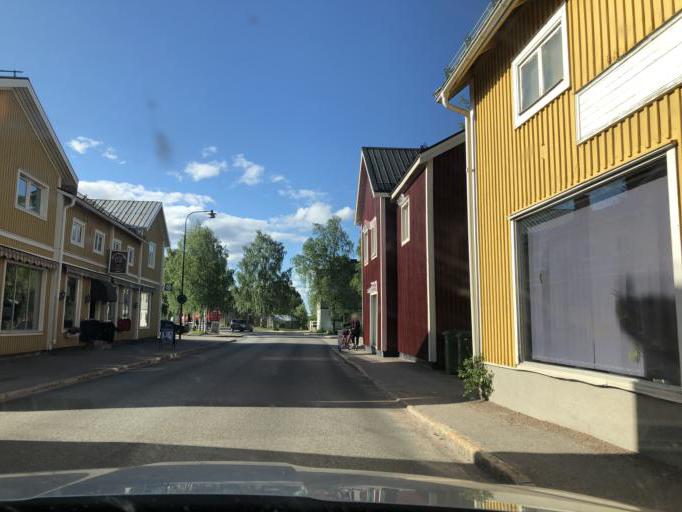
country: SE
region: Norrbotten
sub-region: Overkalix Kommun
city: OEverkalix
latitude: 66.3280
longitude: 22.8438
